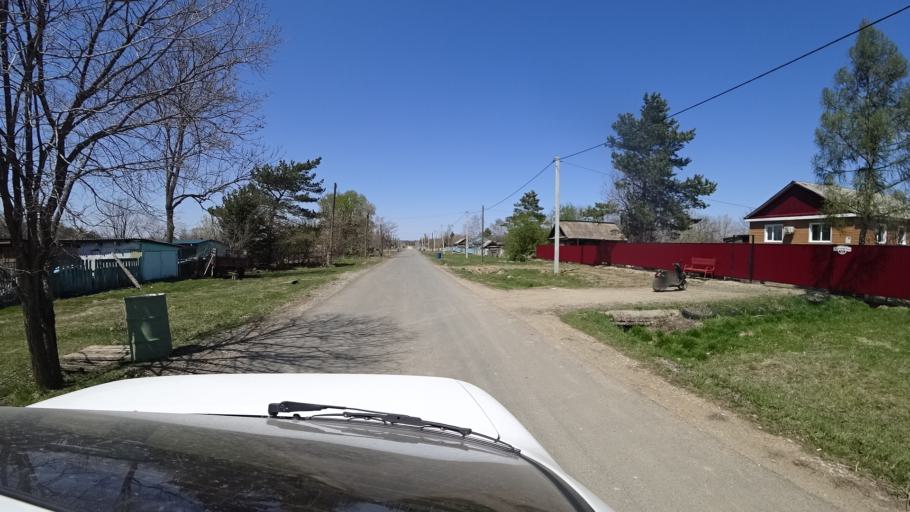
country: RU
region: Primorskiy
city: Dal'nerechensk
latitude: 45.7954
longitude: 133.7710
